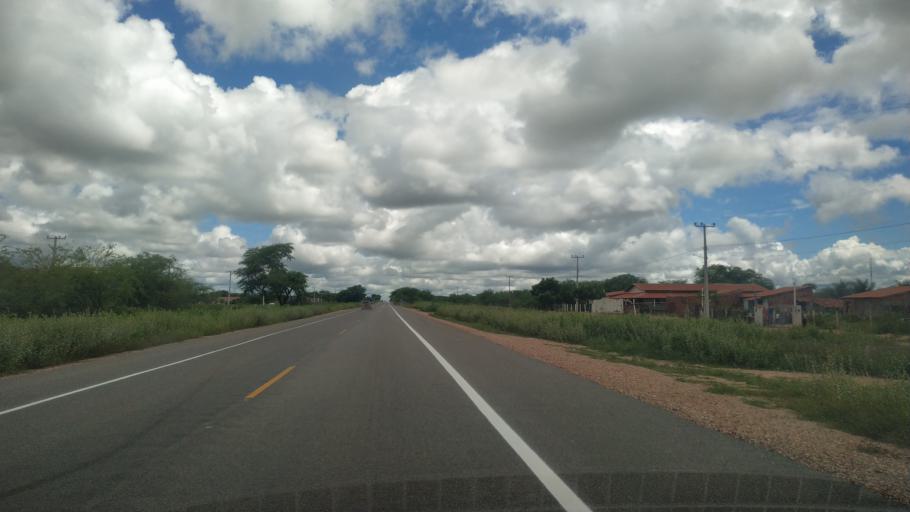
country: BR
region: Rio Grande do Norte
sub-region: Areia Branca
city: Areia Branca
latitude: -5.0552
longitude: -37.1534
